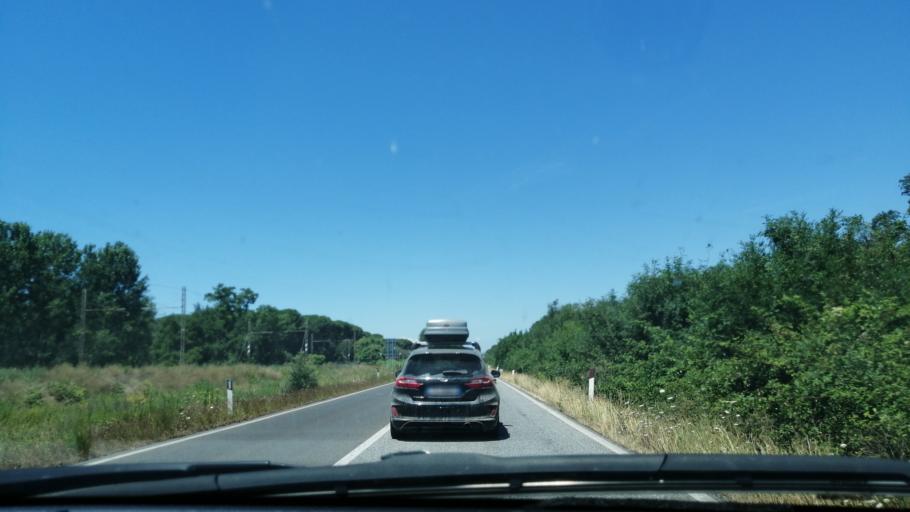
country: IT
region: Tuscany
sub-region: Province of Pisa
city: Migliarino
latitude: 43.7884
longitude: 10.3221
